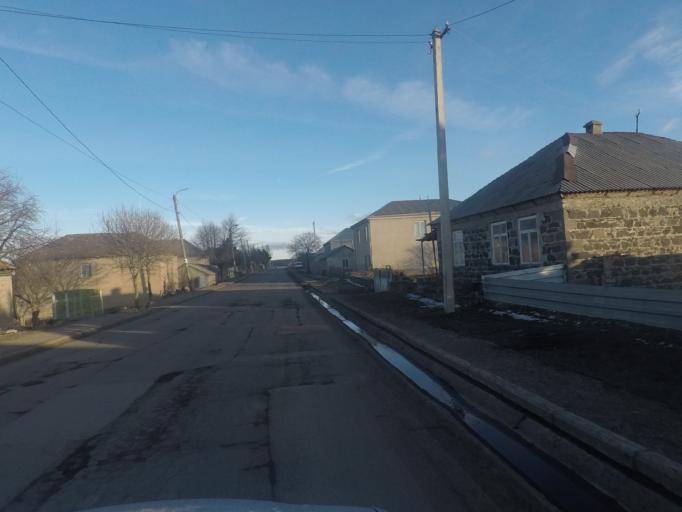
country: GE
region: Kvemo Kartli
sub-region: Tsalka
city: Tsalka
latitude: 41.6034
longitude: 44.0490
